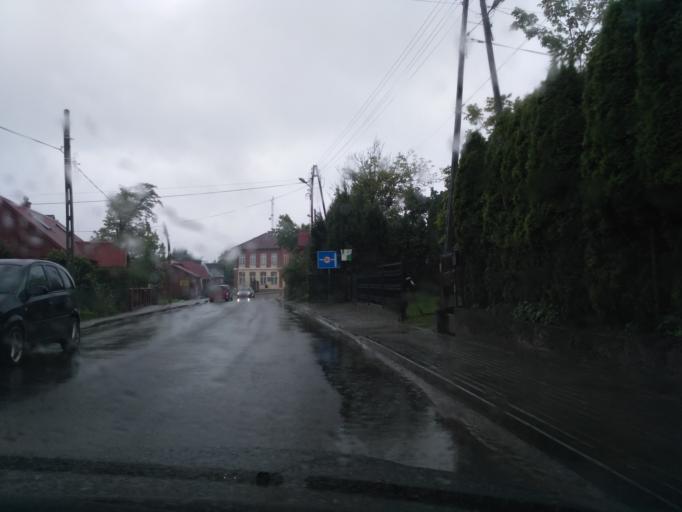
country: PL
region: Subcarpathian Voivodeship
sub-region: Powiat jasielski
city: Debowiec
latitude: 49.6838
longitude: 21.4607
